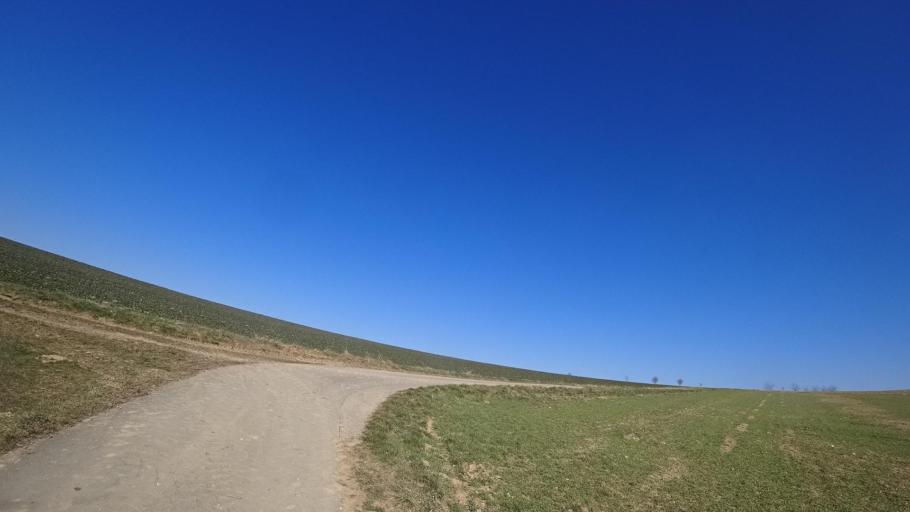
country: DE
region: Rheinland-Pfalz
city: Ravengiersburg
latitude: 49.9375
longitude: 7.4950
